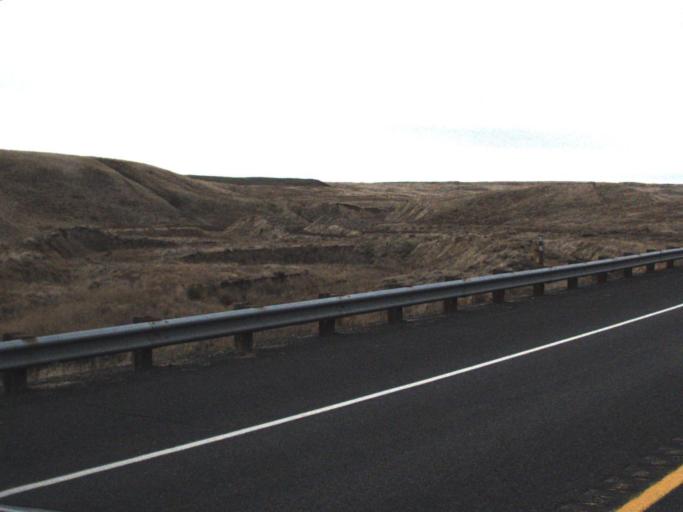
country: US
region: Washington
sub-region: Columbia County
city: Dayton
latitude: 46.7657
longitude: -118.0033
